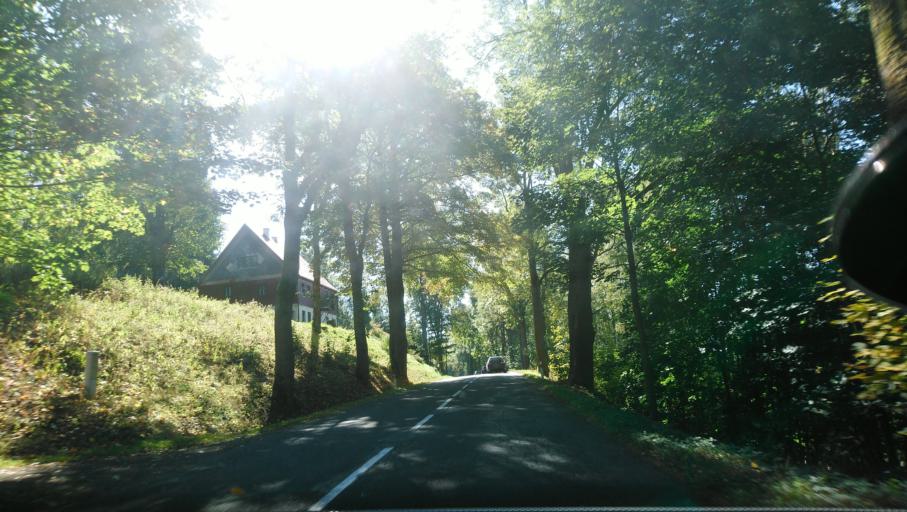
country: CZ
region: Ustecky
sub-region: Okres Chomutov
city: Vejprty
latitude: 50.4749
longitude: 13.0211
